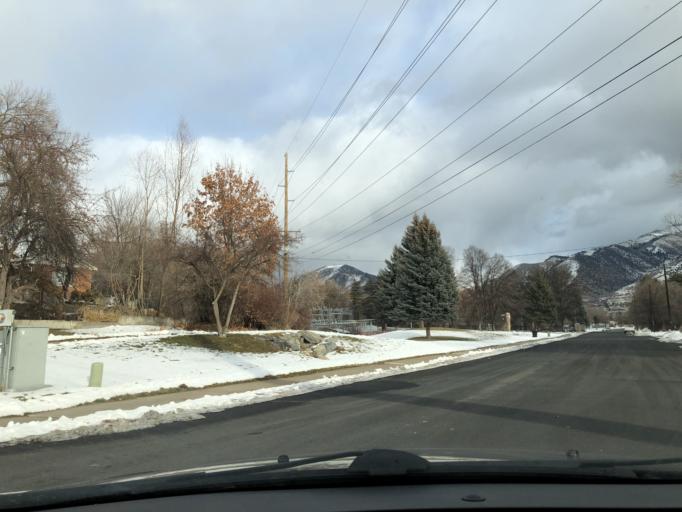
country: US
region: Utah
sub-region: Cache County
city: Logan
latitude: 41.7294
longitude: -111.8323
